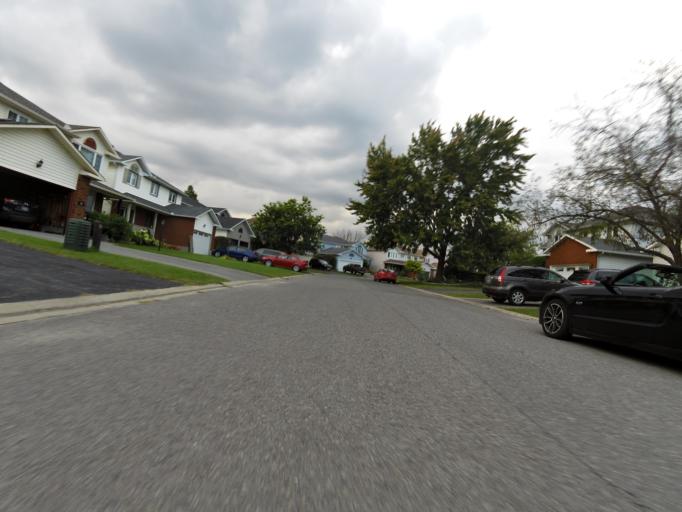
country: CA
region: Ontario
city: Bells Corners
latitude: 45.2646
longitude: -75.7610
